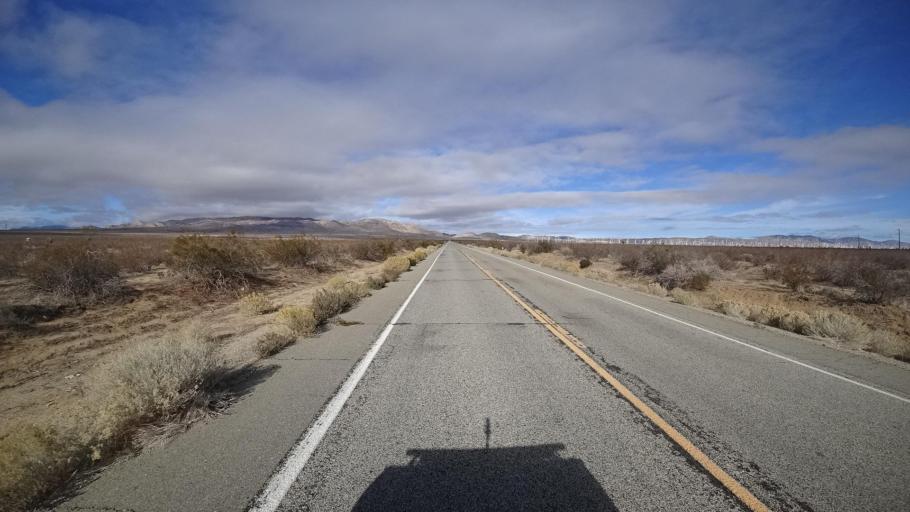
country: US
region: California
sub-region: Kern County
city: Mojave
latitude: 34.9613
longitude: -118.2948
